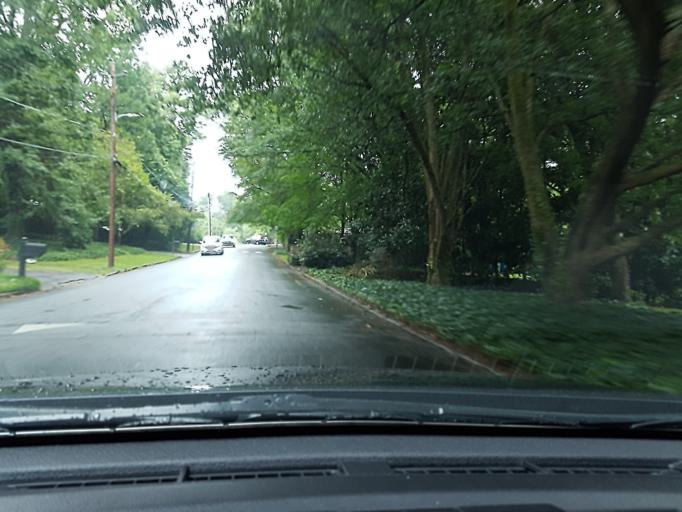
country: US
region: Georgia
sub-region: DeKalb County
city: North Atlanta
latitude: 33.8612
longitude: -84.3828
